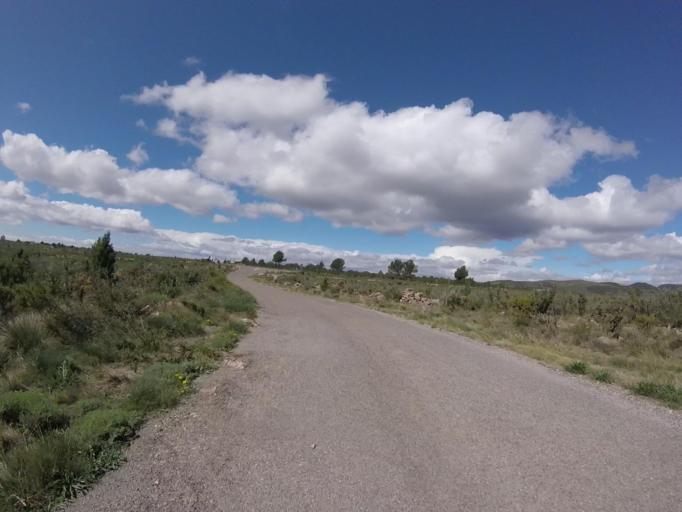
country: ES
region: Valencia
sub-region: Provincia de Castello
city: Culla
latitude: 40.3056
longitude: -0.1228
